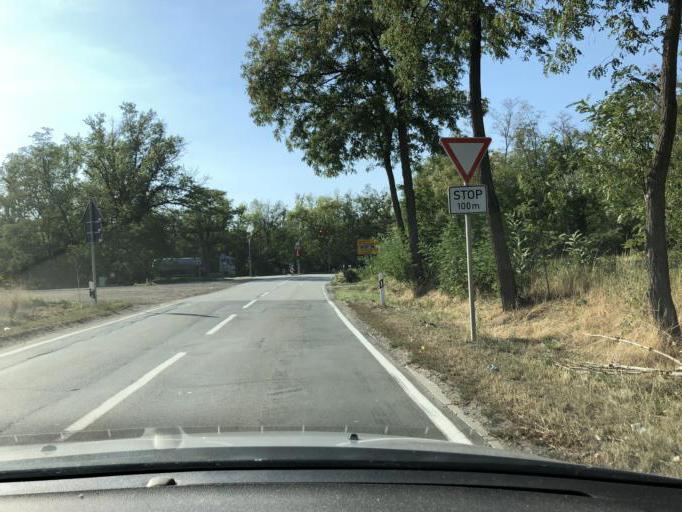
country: DE
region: Saxony-Anhalt
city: Grosskayna
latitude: 51.2937
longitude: 11.9167
